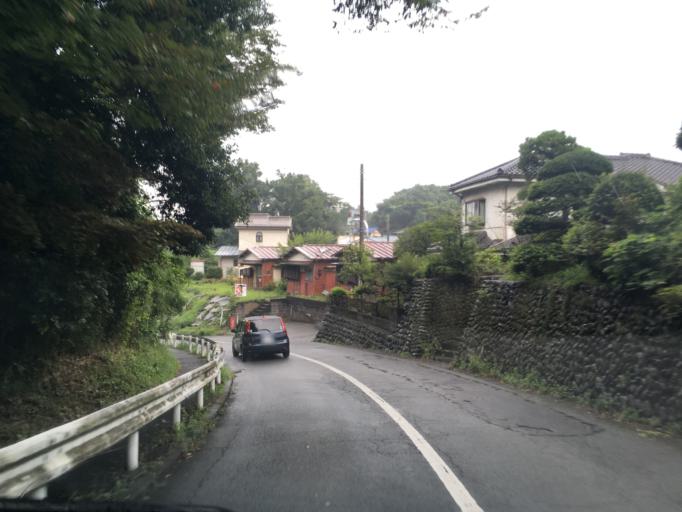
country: JP
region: Tokyo
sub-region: Machida-shi
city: Machida
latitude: 35.6055
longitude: 139.4277
